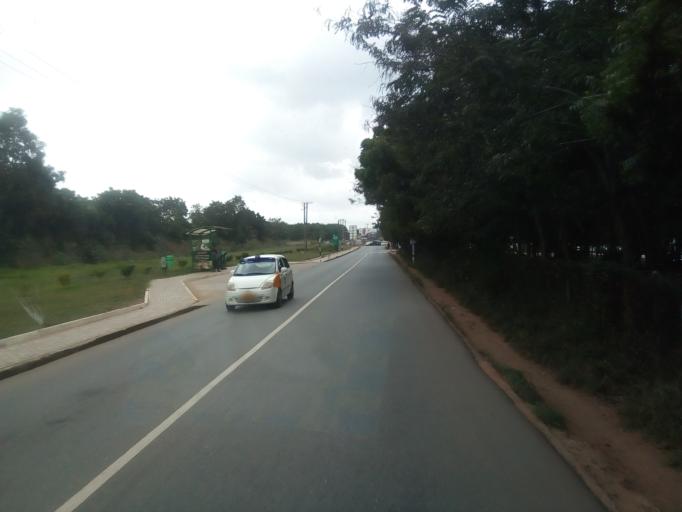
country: GH
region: Greater Accra
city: Dome
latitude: 5.6398
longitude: -0.2078
